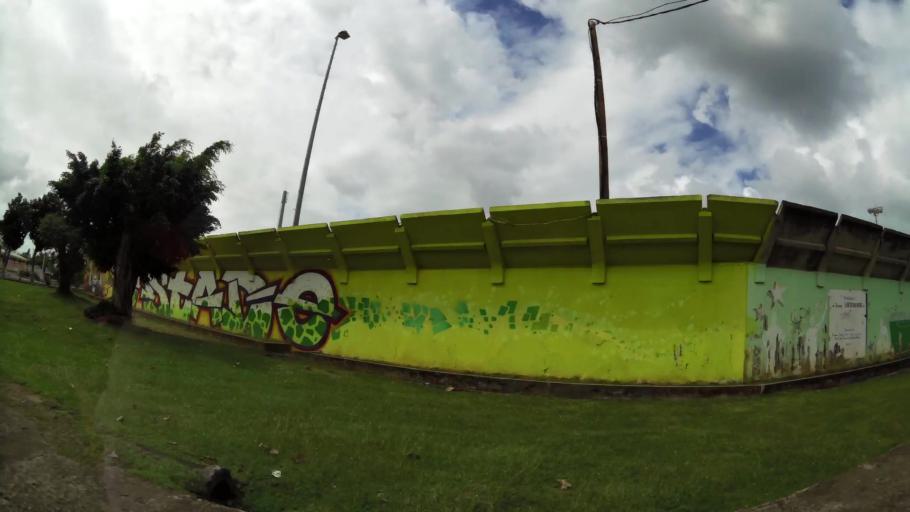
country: GP
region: Guadeloupe
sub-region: Guadeloupe
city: Baie-Mahault
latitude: 16.2628
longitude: -61.5892
